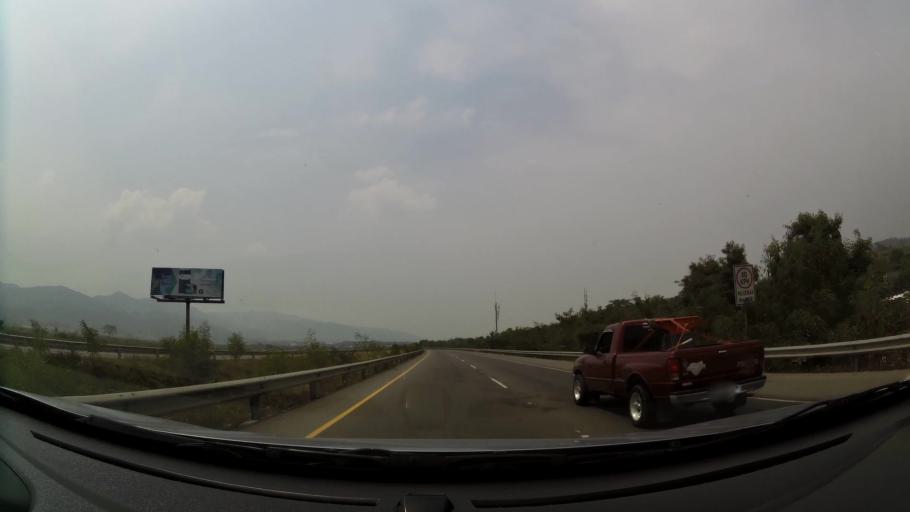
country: HN
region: Cortes
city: El Plan
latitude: 15.2882
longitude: -87.9777
